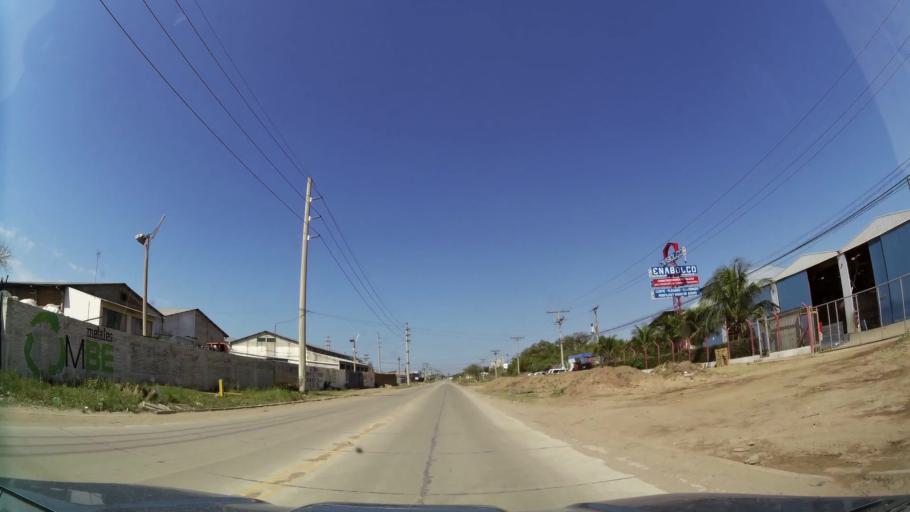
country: BO
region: Santa Cruz
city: Santa Cruz de la Sierra
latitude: -17.7552
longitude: -63.1477
